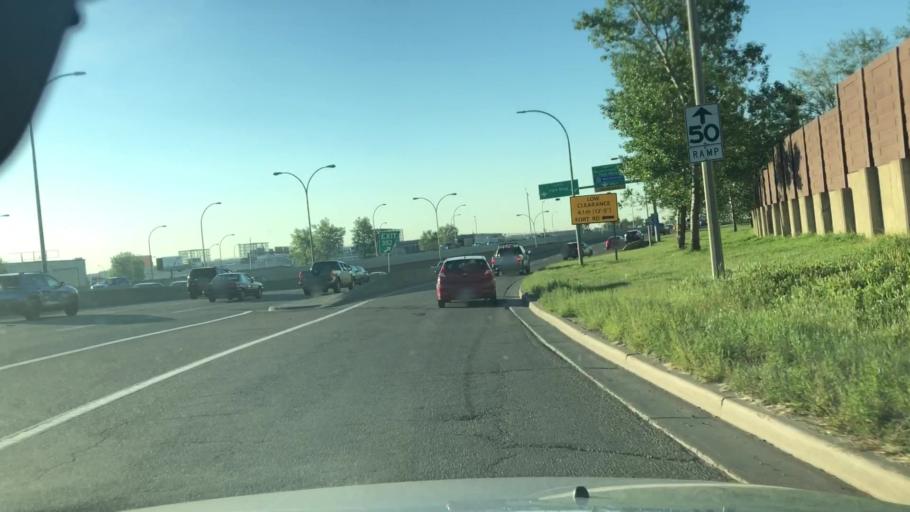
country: CA
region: Alberta
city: Edmonton
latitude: 53.5821
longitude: -113.4558
